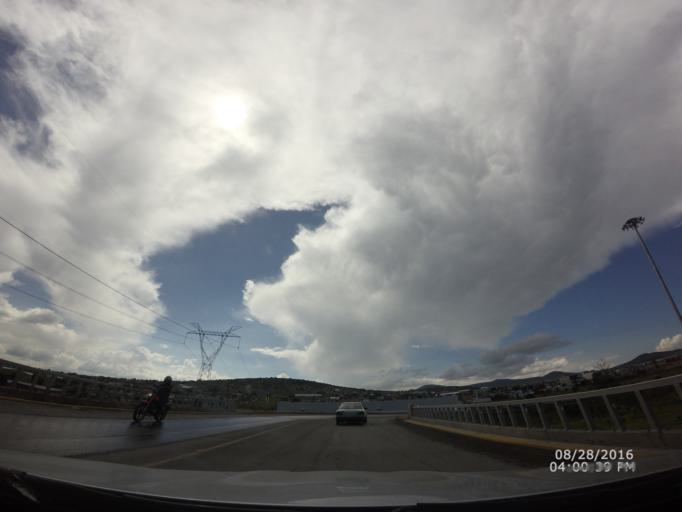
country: MX
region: Hidalgo
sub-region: Zempoala
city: Lindavista
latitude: 20.0402
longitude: -98.7956
